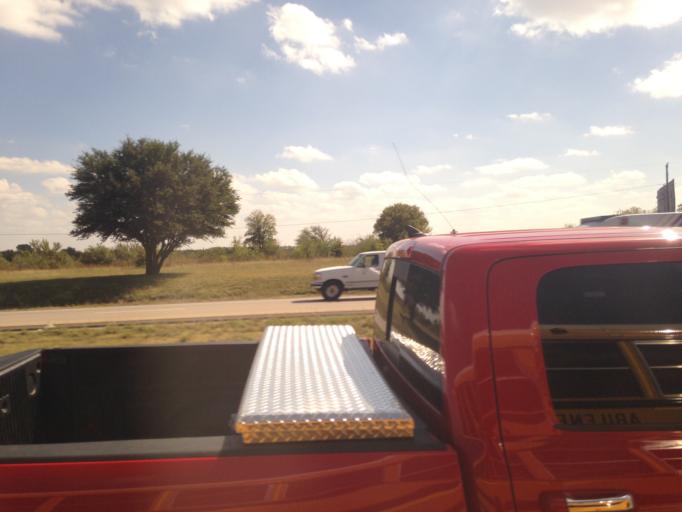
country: US
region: Texas
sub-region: Tarrant County
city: White Settlement
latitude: 32.7269
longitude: -97.5097
